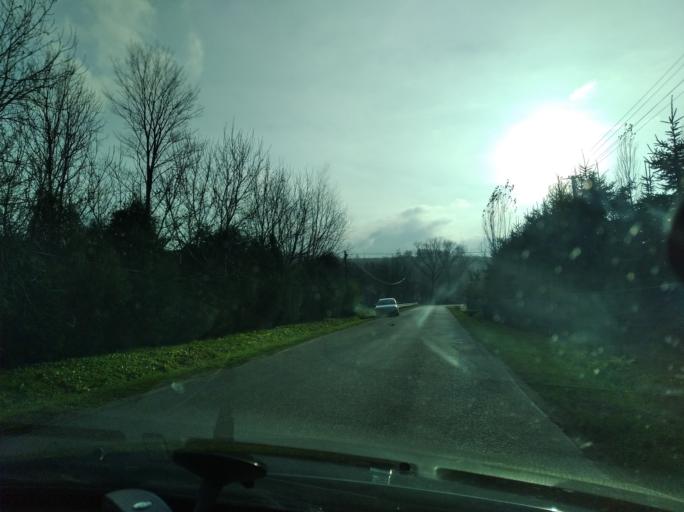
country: PL
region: Subcarpathian Voivodeship
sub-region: Powiat przeworski
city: Lopuszka Wielka
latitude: 49.9403
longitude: 22.4019
